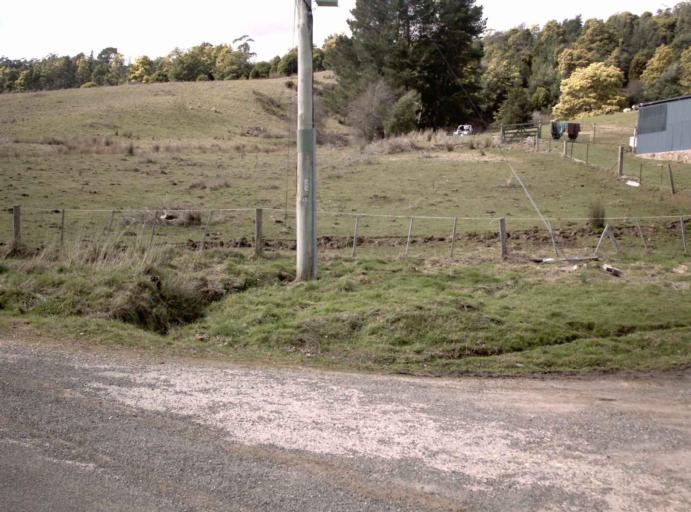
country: AU
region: Tasmania
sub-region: Launceston
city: Mayfield
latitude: -41.2526
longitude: 147.2449
